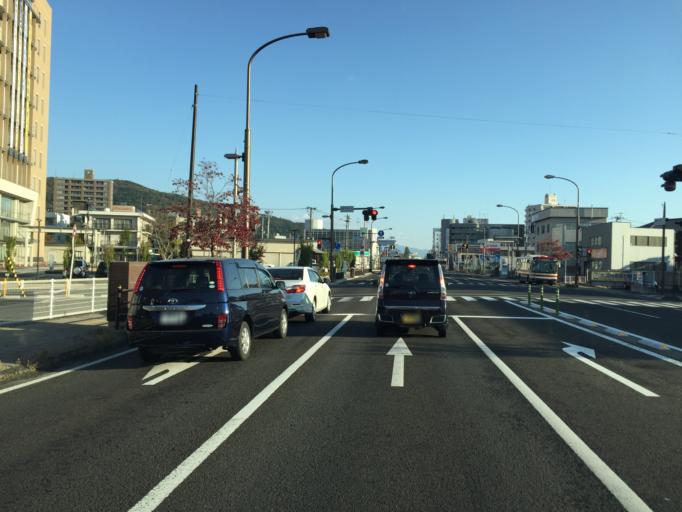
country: JP
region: Fukushima
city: Fukushima-shi
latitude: 37.7600
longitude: 140.4754
